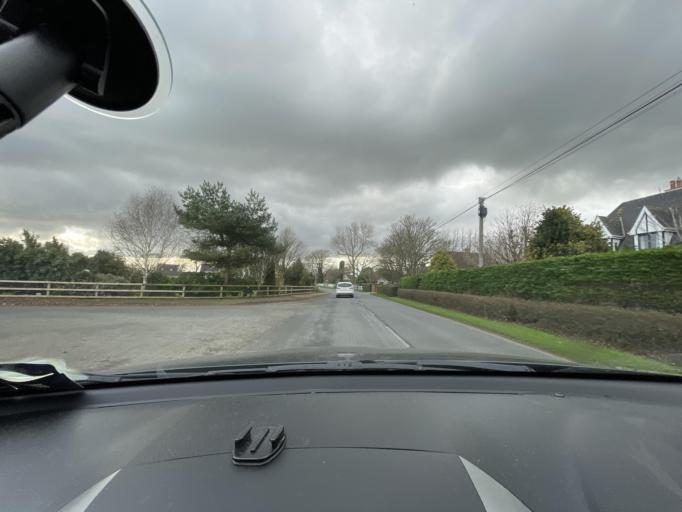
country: IE
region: Leinster
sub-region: Lu
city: Termonfeckin
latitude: 53.7651
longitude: -6.2606
